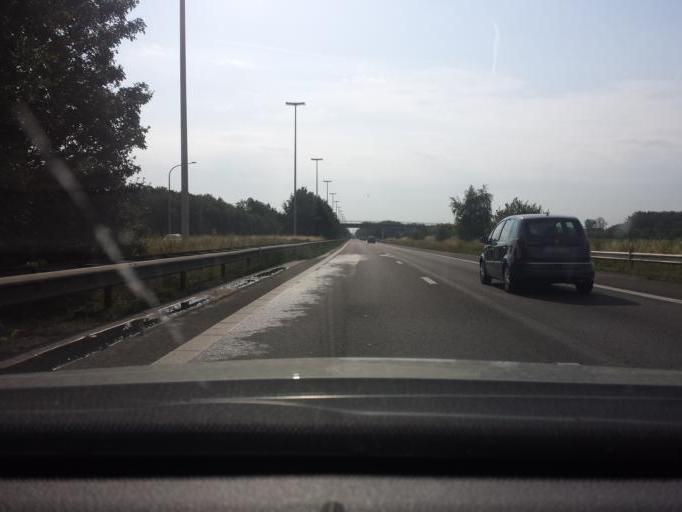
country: BE
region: Flanders
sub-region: Provincie Limburg
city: Hasselt
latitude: 50.9001
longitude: 5.3661
